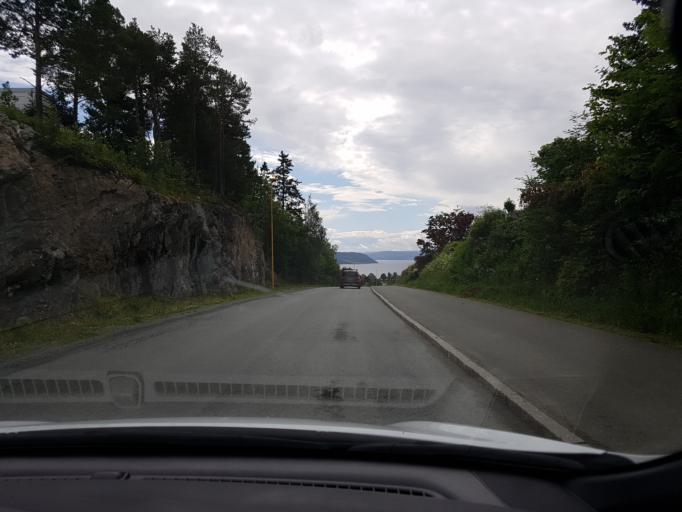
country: NO
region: Nord-Trondelag
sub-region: Frosta
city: Frosta
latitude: 63.5943
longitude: 10.7362
